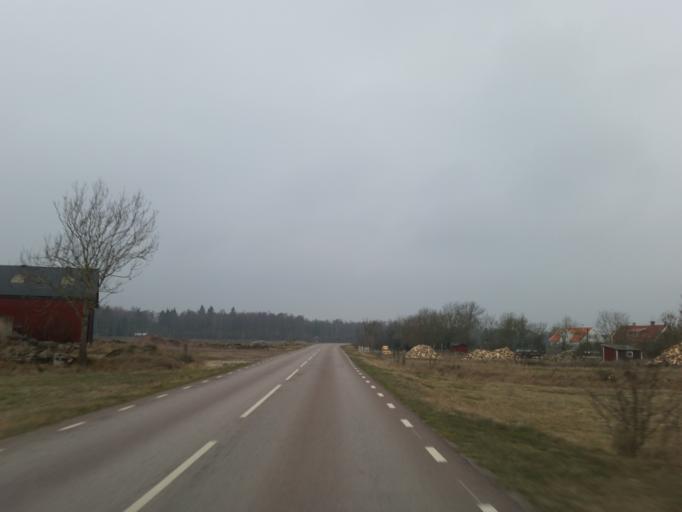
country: SE
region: Kalmar
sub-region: Morbylanga Kommun
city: Sodra Sandby
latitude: 56.6133
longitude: 16.6145
